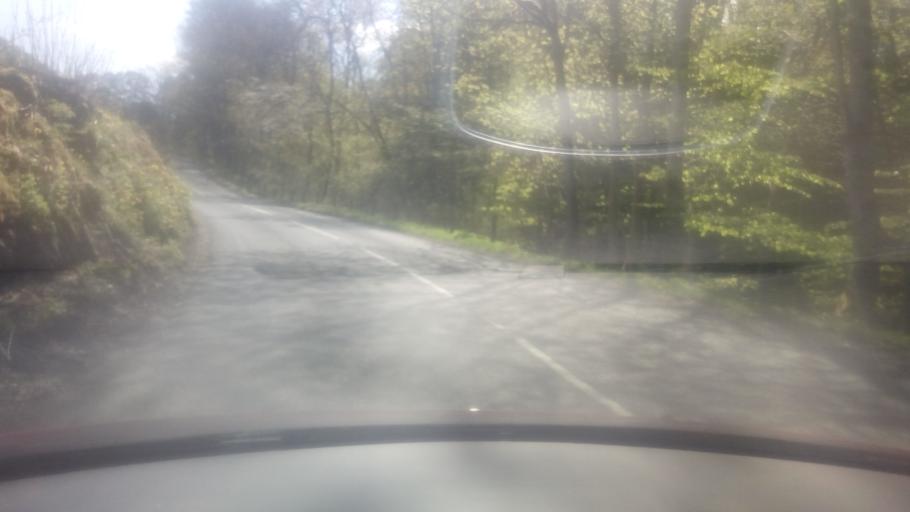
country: GB
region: Scotland
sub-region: The Scottish Borders
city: Hawick
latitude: 55.4211
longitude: -2.7400
